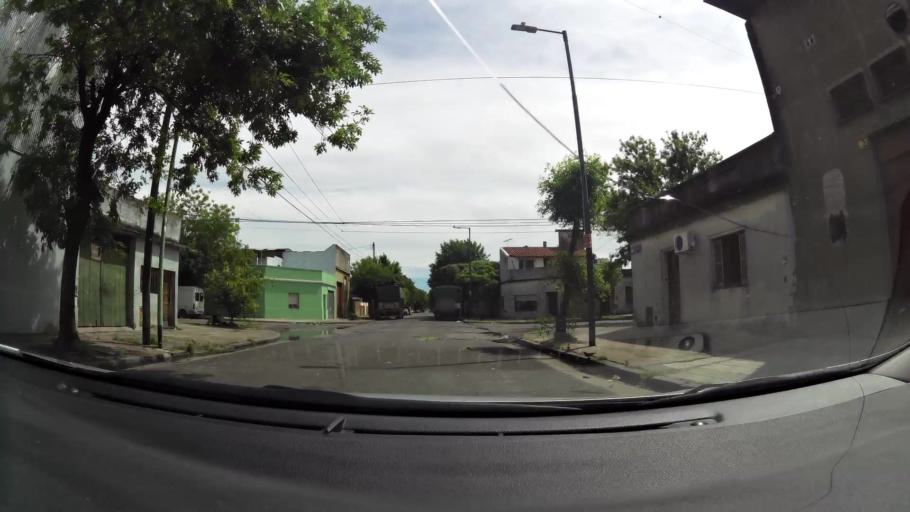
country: AR
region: Buenos Aires F.D.
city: Villa Lugano
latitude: -34.6625
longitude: -58.4280
